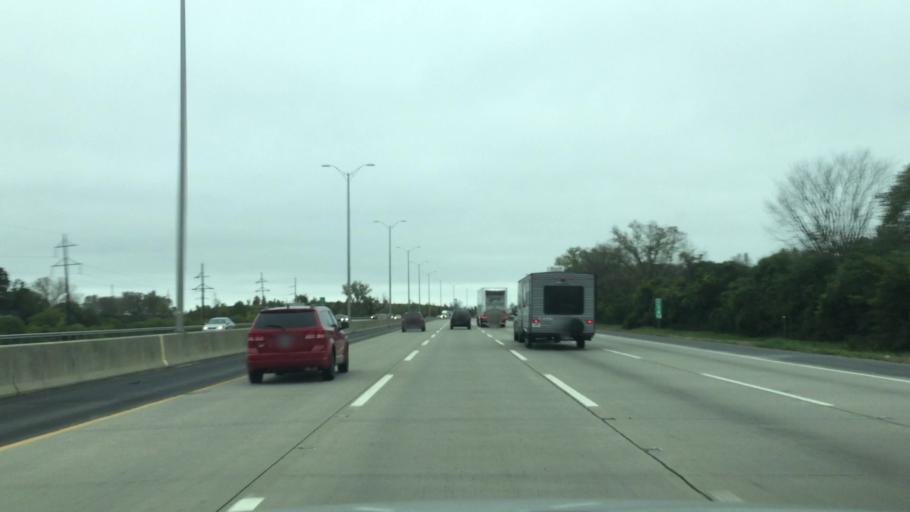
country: US
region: Illinois
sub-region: Lake County
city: Green Oaks
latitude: 42.3018
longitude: -87.9034
